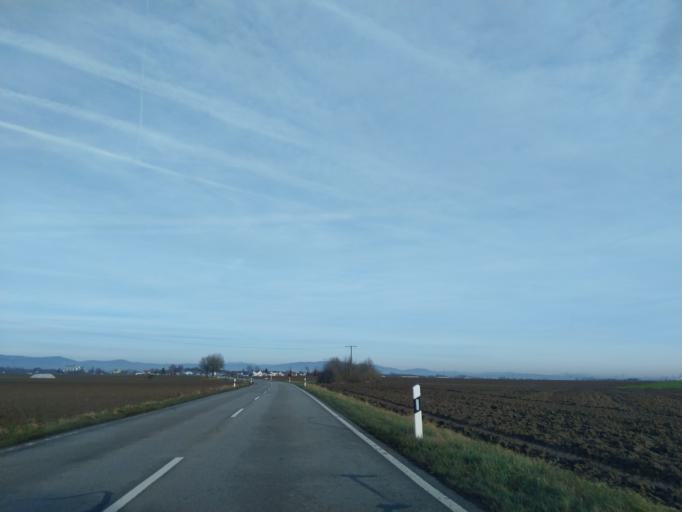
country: DE
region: Bavaria
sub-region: Lower Bavaria
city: Buchhofen
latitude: 48.6874
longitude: 12.9091
